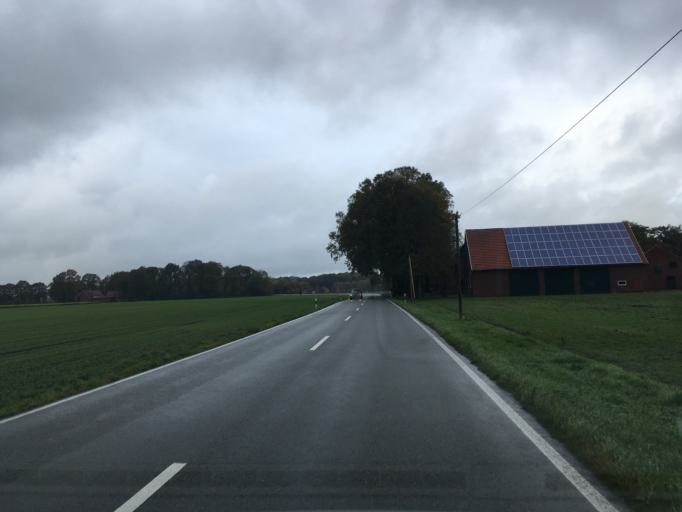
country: DE
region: North Rhine-Westphalia
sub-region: Regierungsbezirk Munster
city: Velen
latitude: 51.8722
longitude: 7.0210
